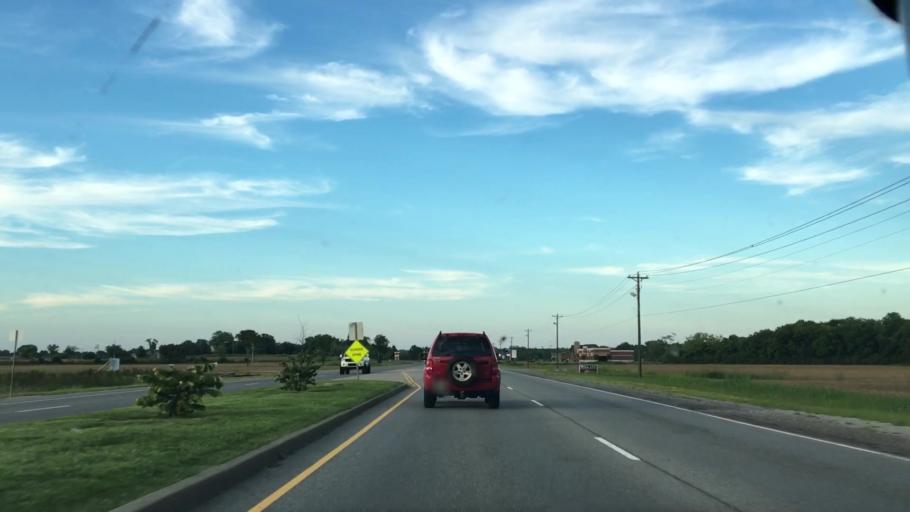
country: US
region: Tennessee
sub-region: Wilson County
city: Lebanon
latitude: 36.1991
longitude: -86.3319
